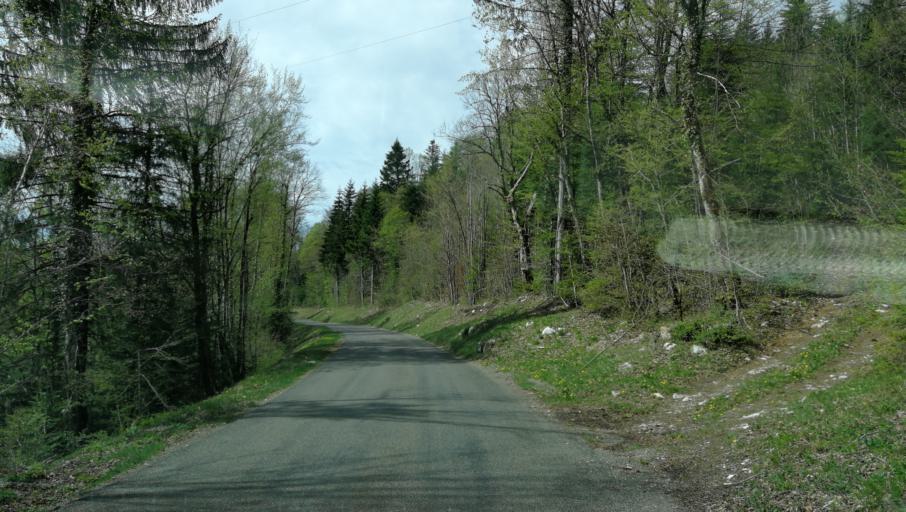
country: FR
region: Rhone-Alpes
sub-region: Departement de l'Ain
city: Arbent
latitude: 46.2338
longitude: 5.7563
